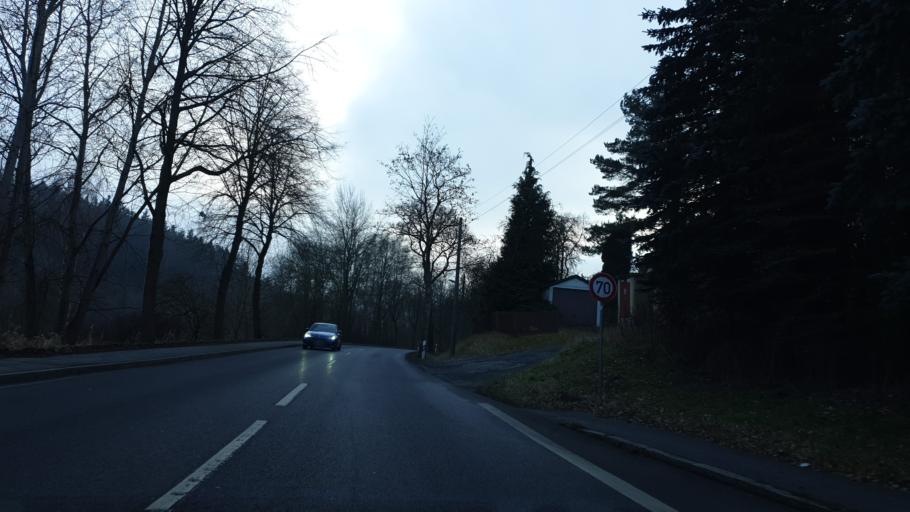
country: DE
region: Saxony
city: Adorf
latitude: 50.3000
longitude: 12.2512
